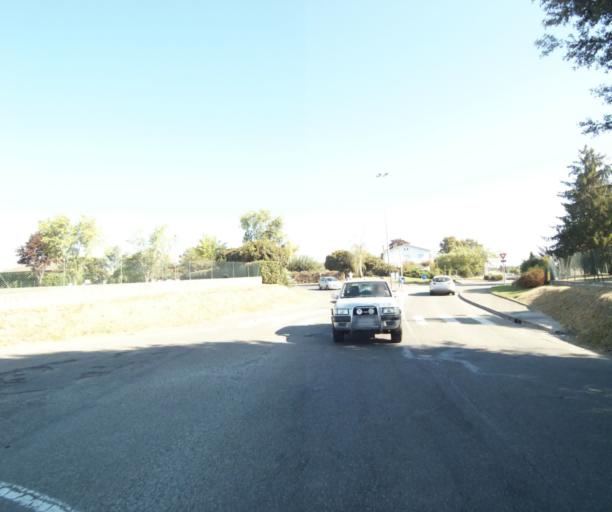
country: FR
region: Midi-Pyrenees
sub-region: Departement du Tarn-et-Garonne
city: Verdun-sur-Garonne
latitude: 43.8530
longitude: 1.2301
